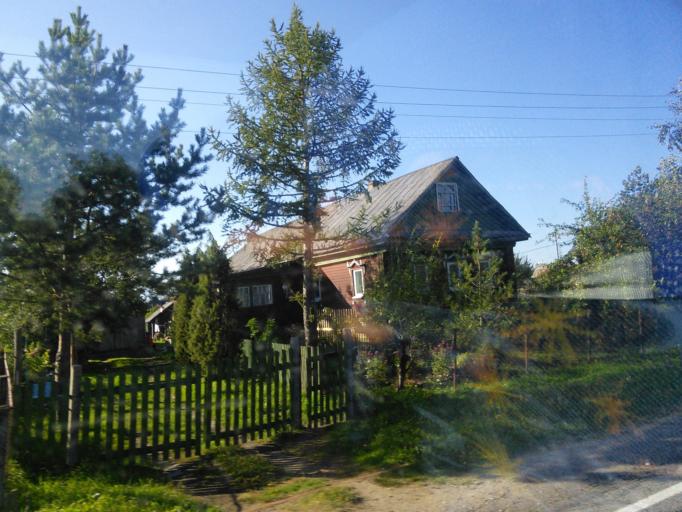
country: RU
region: Jaroslavl
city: Rybinsk
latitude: 58.2619
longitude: 38.8490
